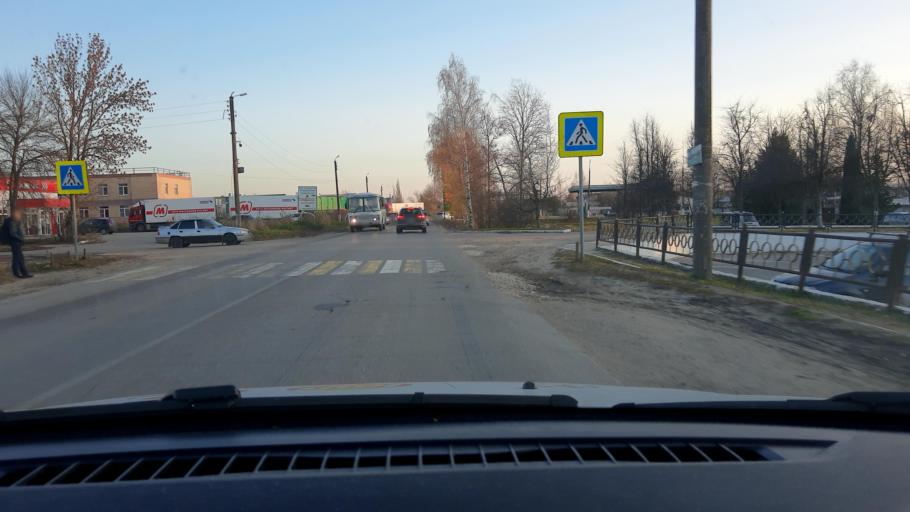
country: RU
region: Nizjnij Novgorod
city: Volodarsk
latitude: 56.2433
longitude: 43.1812
